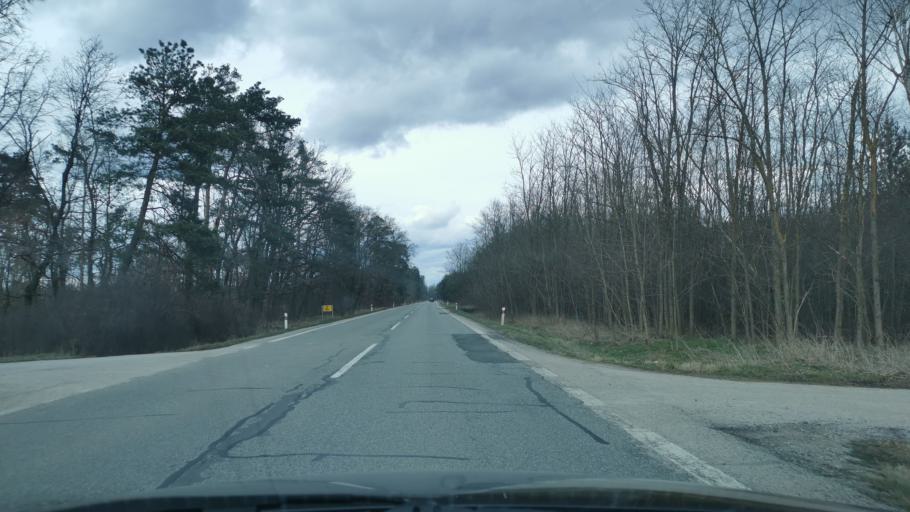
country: SK
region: Trnavsky
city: Gbely
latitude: 48.7613
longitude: 17.0824
